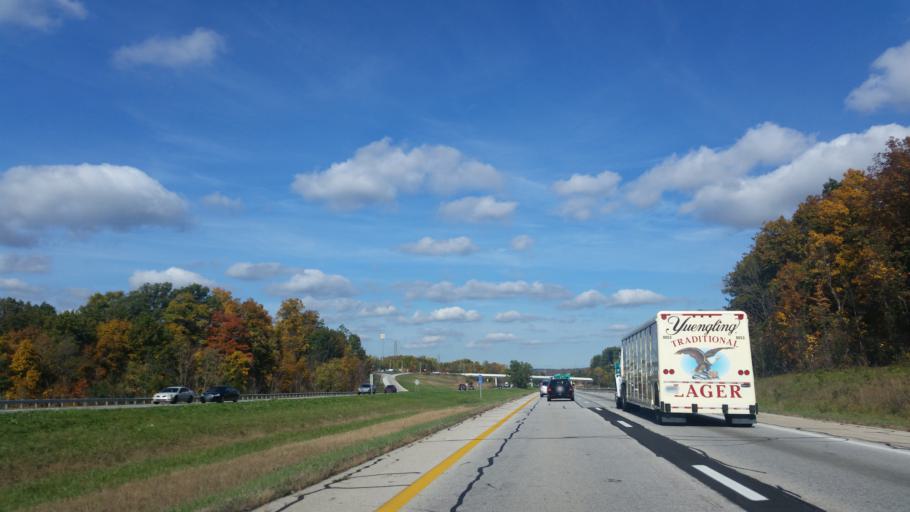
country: US
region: Ohio
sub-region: Summit County
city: Richfield
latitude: 41.2156
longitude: -81.6259
